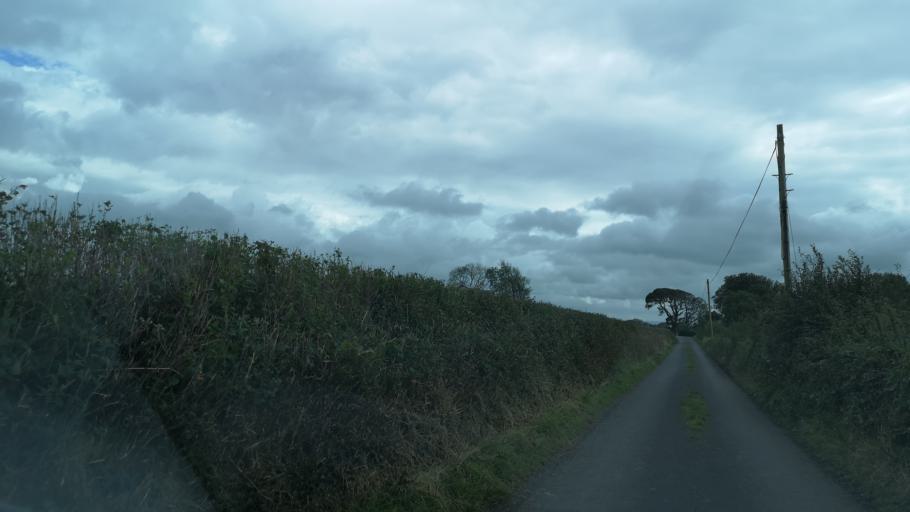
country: IE
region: Connaught
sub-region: County Galway
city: Athenry
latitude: 53.2986
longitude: -8.6827
